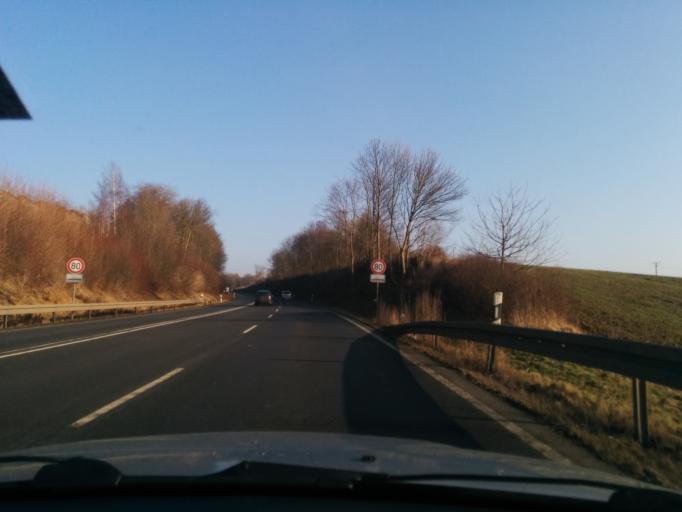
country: DE
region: Hesse
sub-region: Regierungsbezirk Kassel
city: Kaufungen
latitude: 51.2795
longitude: 9.5969
